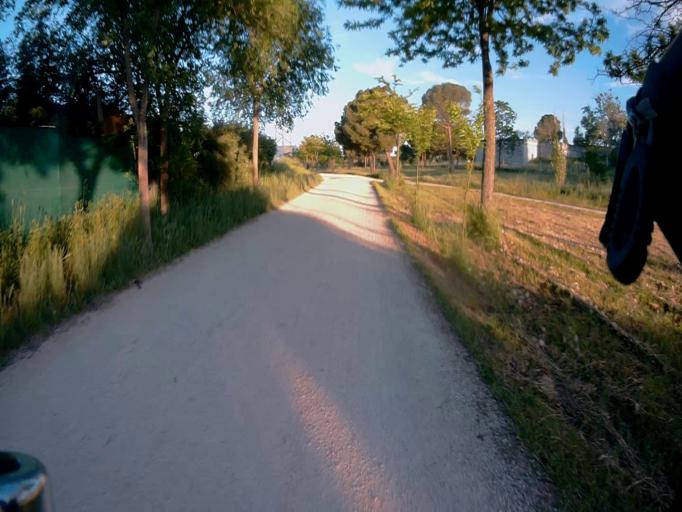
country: ES
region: Madrid
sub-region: Provincia de Madrid
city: Alcorcon
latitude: 40.3298
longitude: -3.7999
